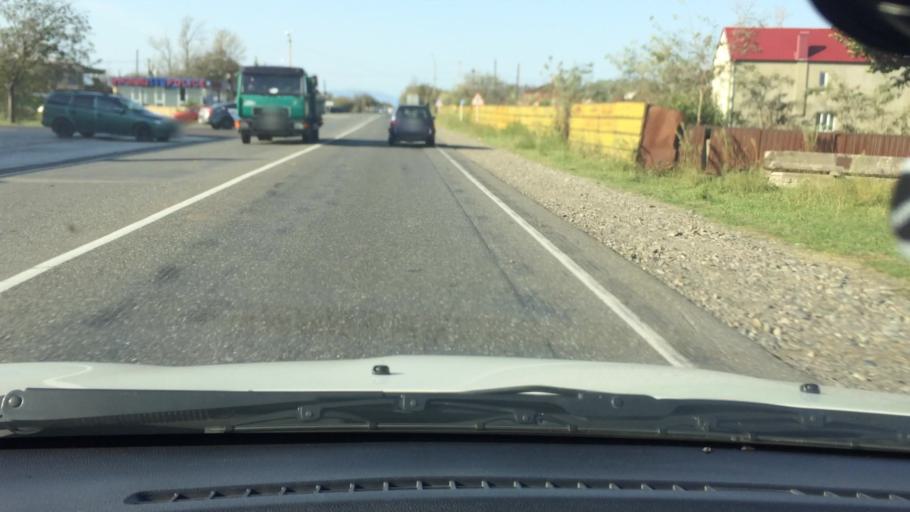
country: GE
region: Imereti
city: Vani
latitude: 42.2099
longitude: 42.5526
